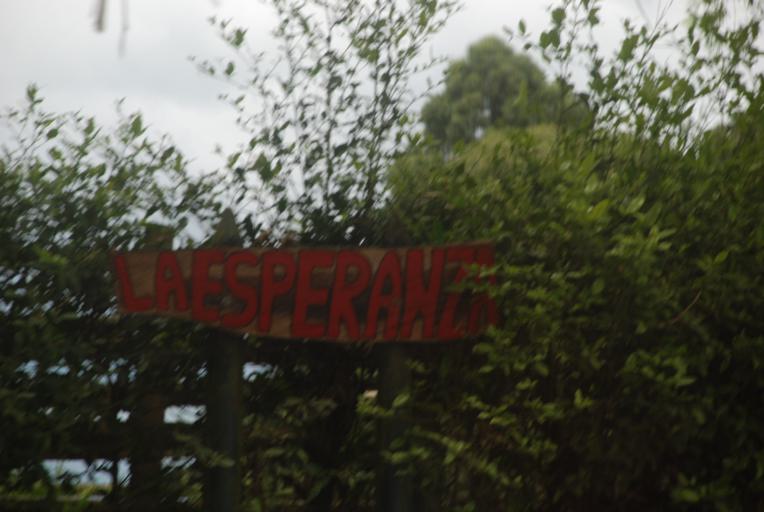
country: CO
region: Quindio
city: Filandia
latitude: 4.7190
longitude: -75.6801
